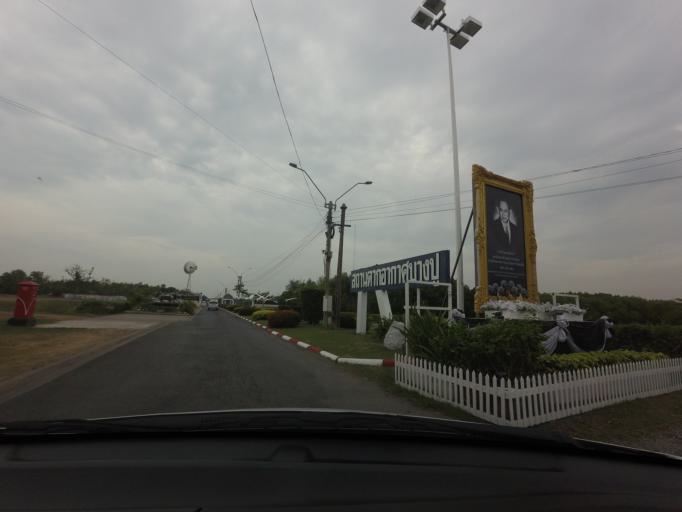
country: TH
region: Samut Prakan
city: Samut Prakan
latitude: 13.5212
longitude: 100.6559
